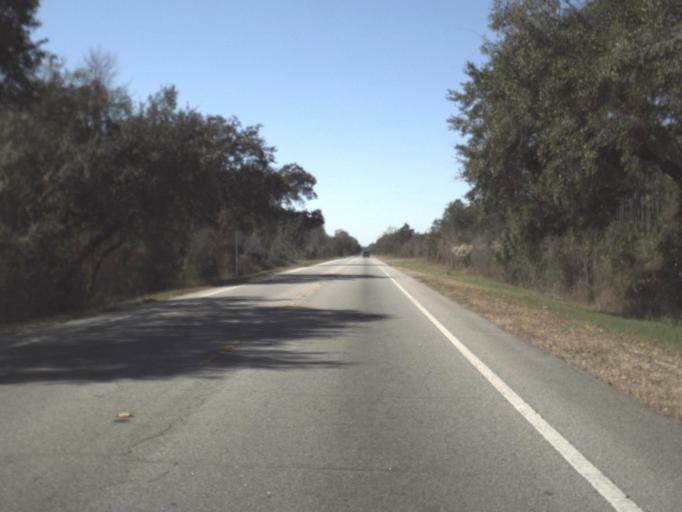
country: US
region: Florida
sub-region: Leon County
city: Woodville
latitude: 30.3414
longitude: -84.3175
